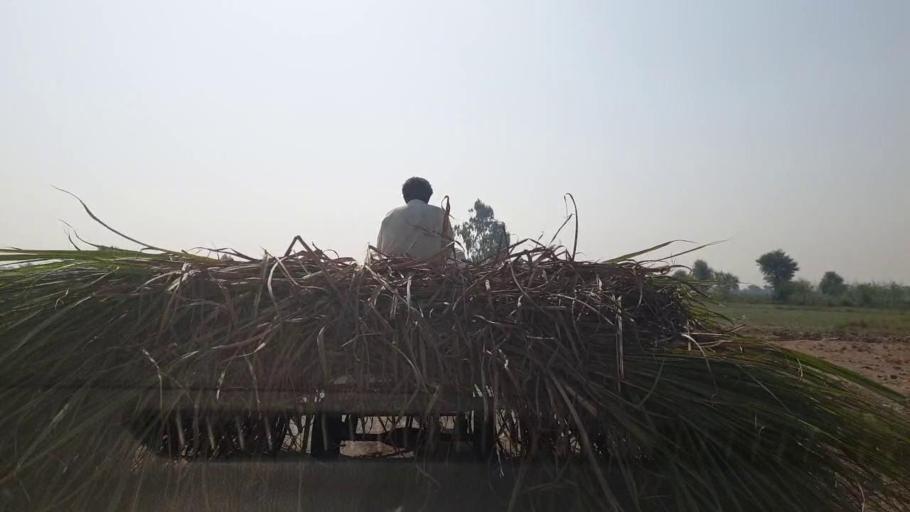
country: PK
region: Sindh
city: Shahdadpur
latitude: 25.9258
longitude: 68.7339
